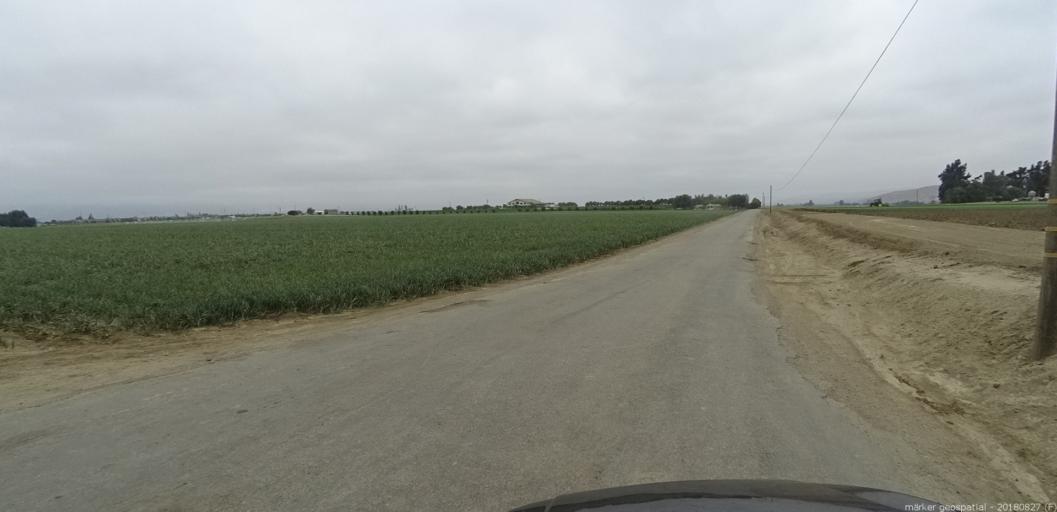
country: US
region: California
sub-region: Monterey County
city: Greenfield
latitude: 36.3314
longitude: -121.2146
